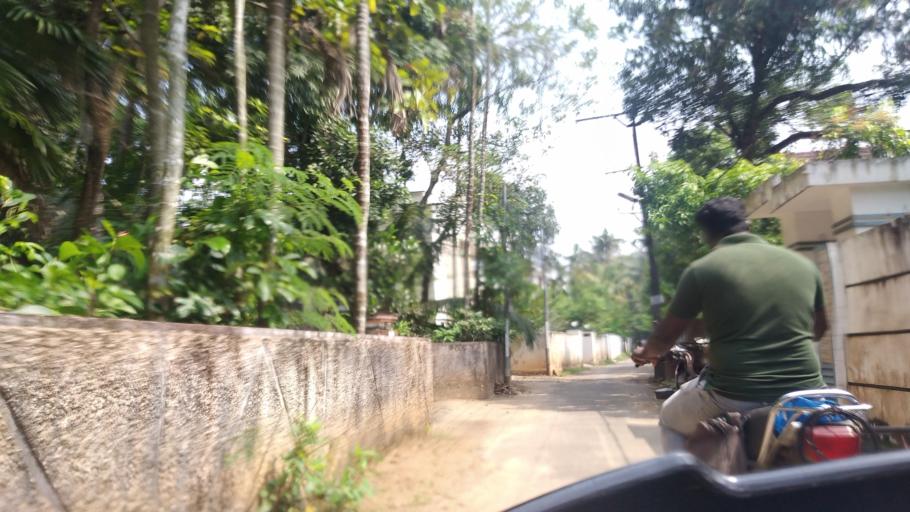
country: IN
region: Kerala
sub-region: Ernakulam
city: Elur
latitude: 10.0574
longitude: 76.2167
